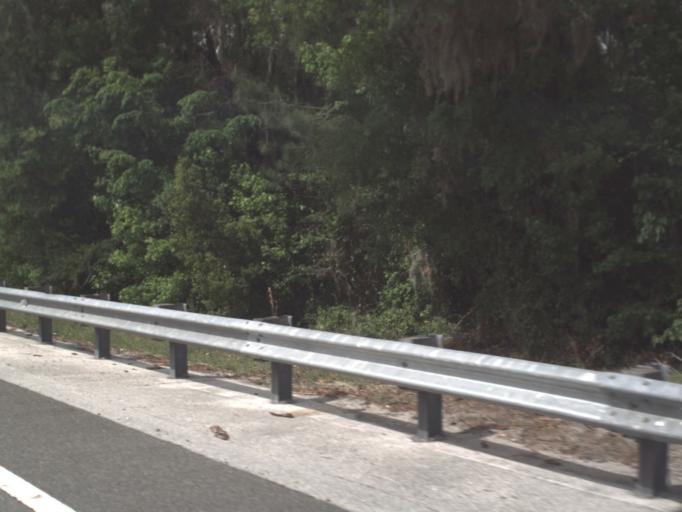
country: US
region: Florida
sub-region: Putnam County
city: Crescent City
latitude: 29.5119
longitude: -81.4982
